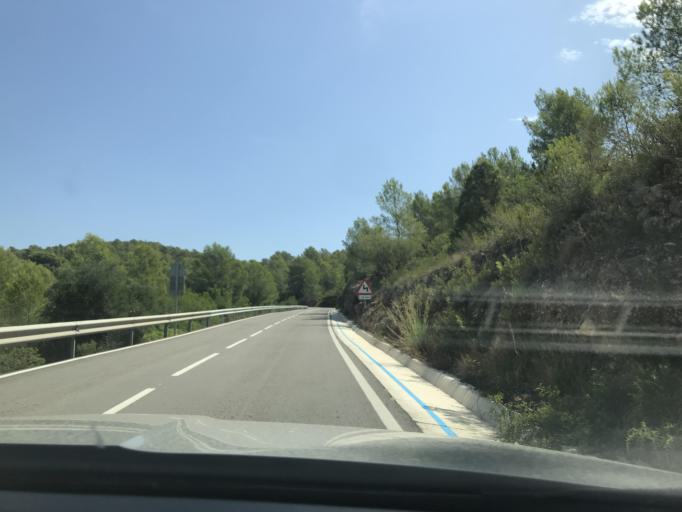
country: ES
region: Catalonia
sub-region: Provincia de Tarragona
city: Salomo
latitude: 41.1904
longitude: 1.3813
